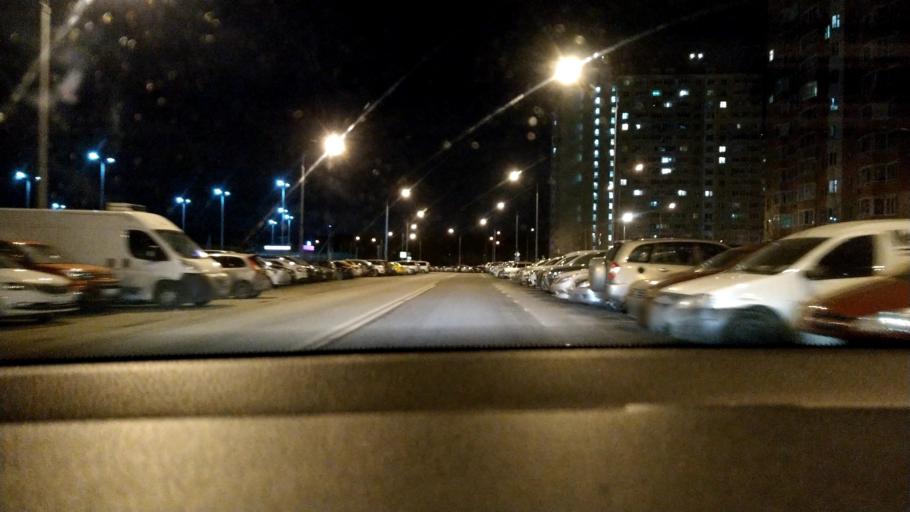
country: RU
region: Moscow
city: Novo-Peredelkino
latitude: 55.6420
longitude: 37.3266
